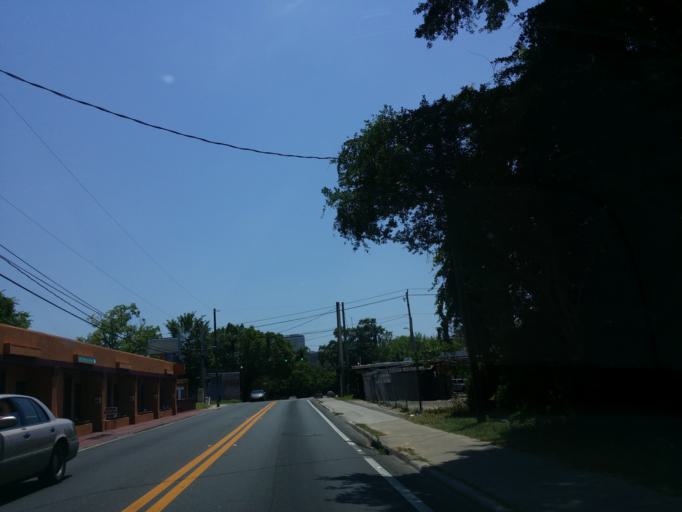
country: US
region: Florida
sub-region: Leon County
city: Tallahassee
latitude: 30.4497
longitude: -84.2895
